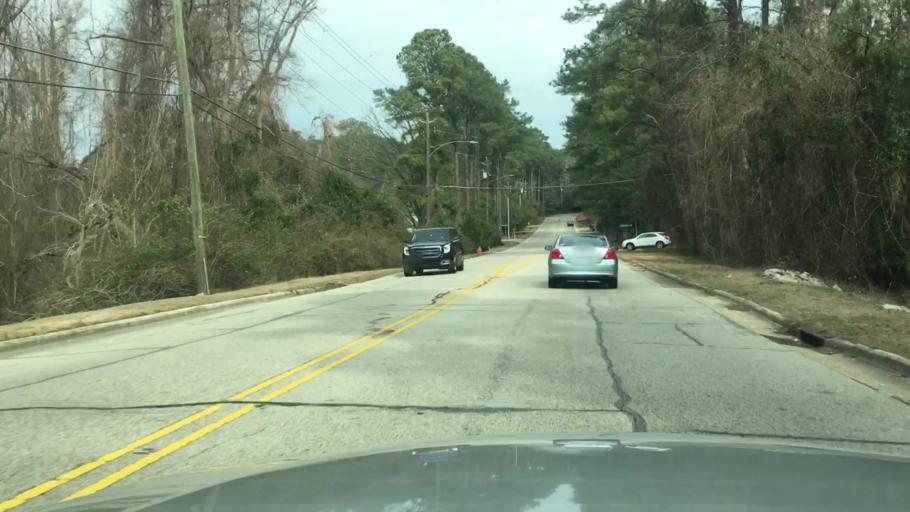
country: US
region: North Carolina
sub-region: Cumberland County
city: Fayetteville
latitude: 35.0501
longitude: -78.9141
